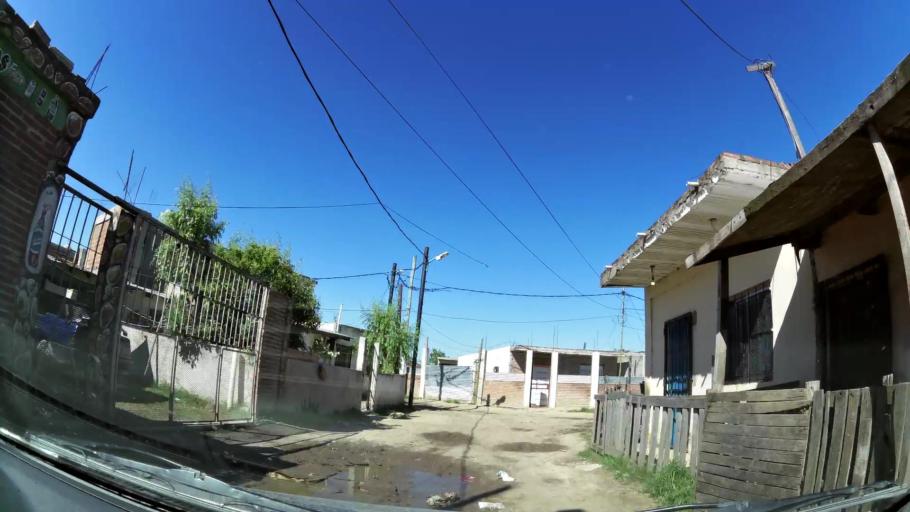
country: AR
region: Buenos Aires
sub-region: Partido de Quilmes
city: Quilmes
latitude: -34.7067
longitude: -58.3032
